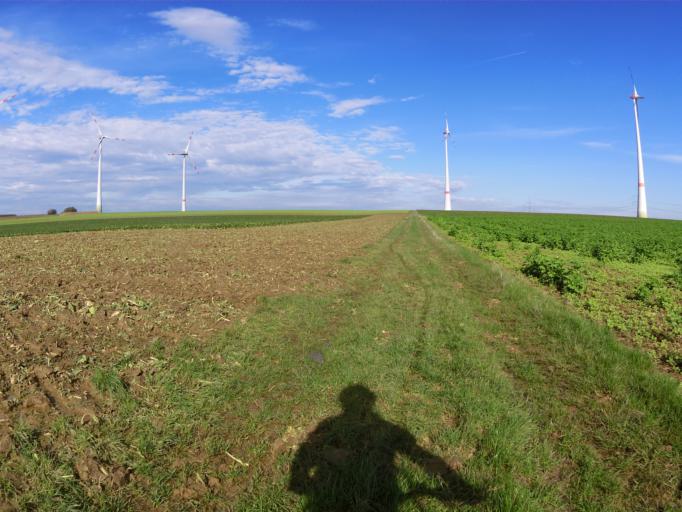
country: DE
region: Bavaria
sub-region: Regierungsbezirk Unterfranken
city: Sommerhausen
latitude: 49.7128
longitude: 10.0505
